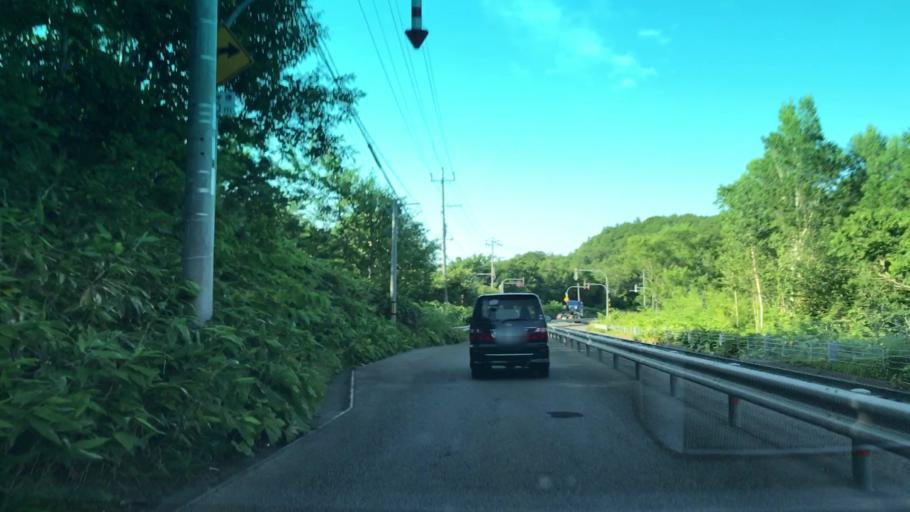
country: JP
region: Hokkaido
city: Otaru
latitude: 43.1438
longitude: 141.0119
